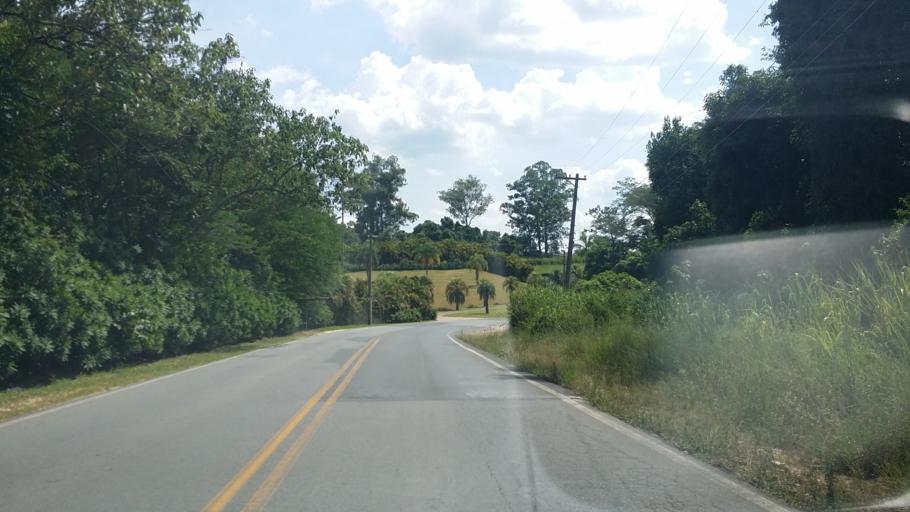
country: BR
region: Sao Paulo
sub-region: Itupeva
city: Itupeva
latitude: -23.1921
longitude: -47.0854
